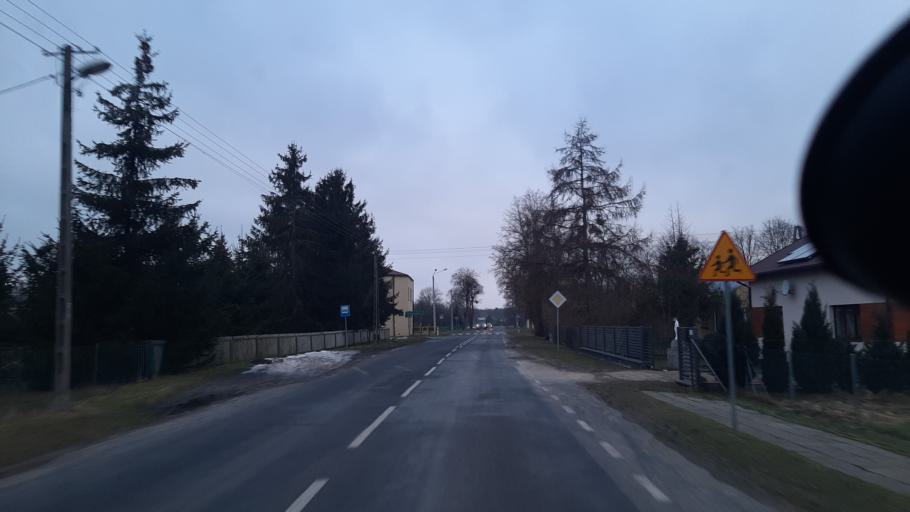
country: PL
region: Lublin Voivodeship
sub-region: Powiat parczewski
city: Debowa Kloda
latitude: 51.6382
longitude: 23.0367
